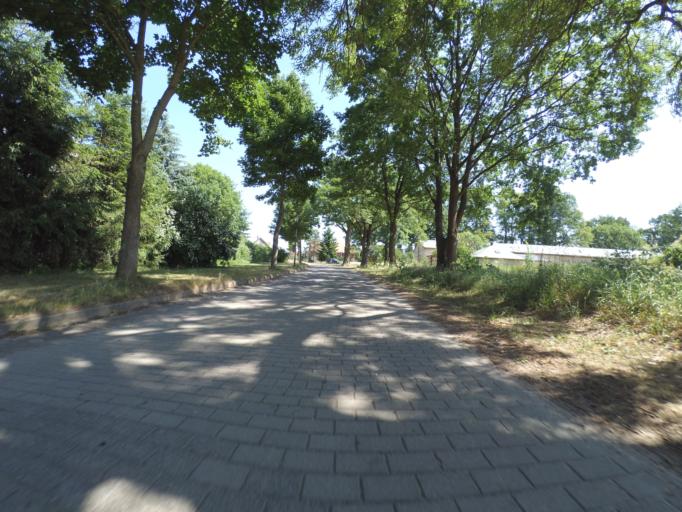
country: DE
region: Brandenburg
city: Heiligengrabe
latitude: 53.2000
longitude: 12.3331
